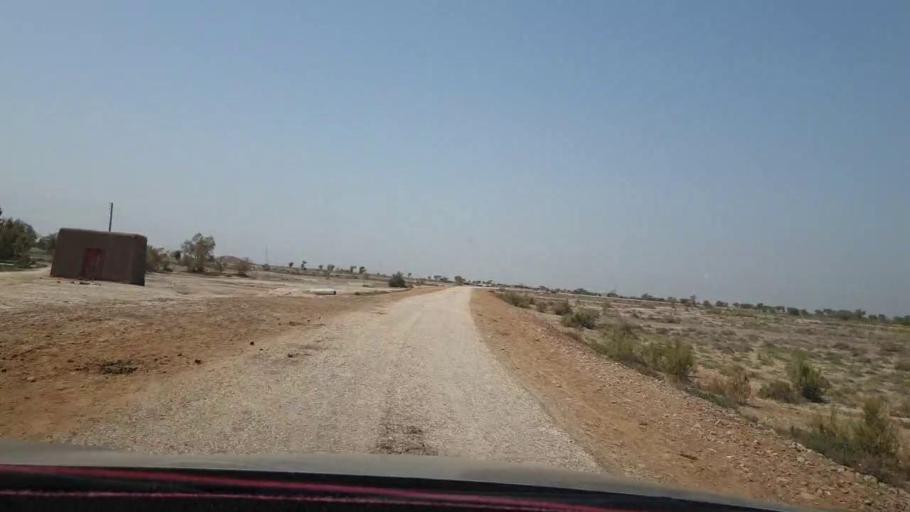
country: PK
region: Sindh
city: Warah
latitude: 27.5045
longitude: 67.7074
